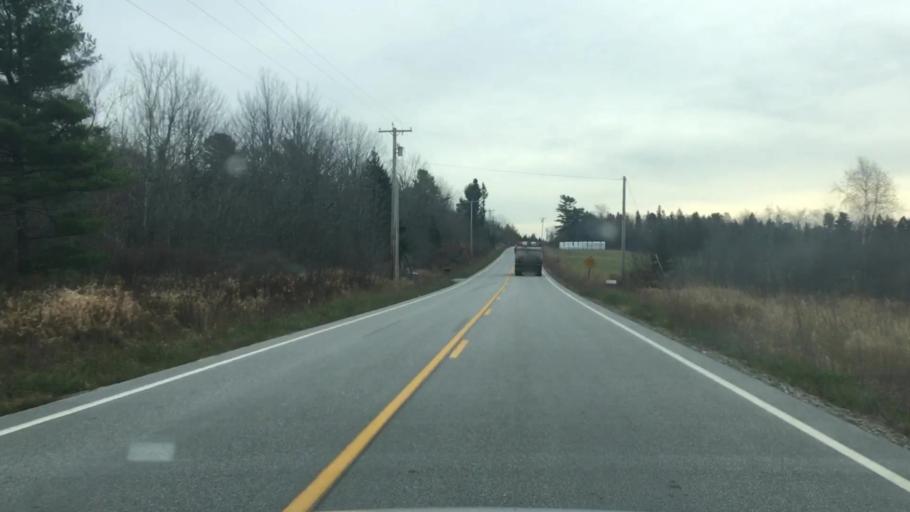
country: US
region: Maine
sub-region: Hancock County
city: Orland
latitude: 44.5299
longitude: -68.6729
